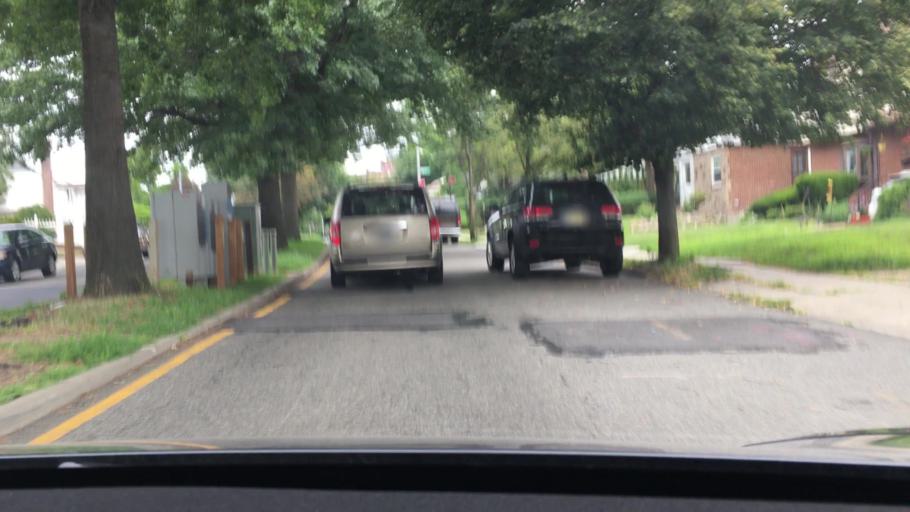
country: US
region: New York
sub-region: Queens County
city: Jamaica
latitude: 40.7380
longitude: -73.7901
